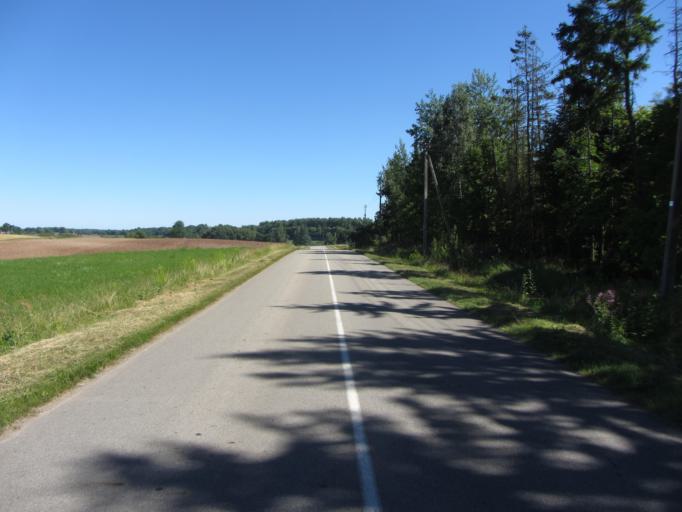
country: LT
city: Kupiskis
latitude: 55.8405
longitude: 25.0442
